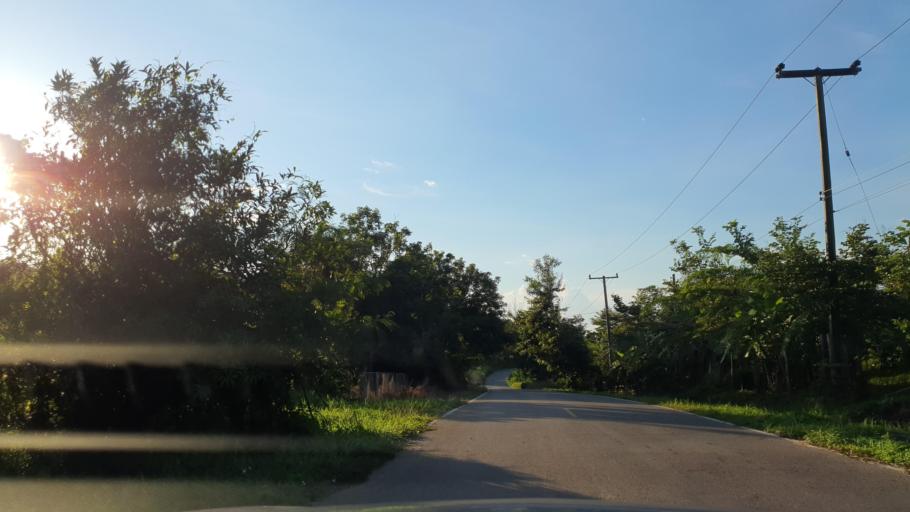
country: TH
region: Chiang Mai
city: Mae On
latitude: 18.8303
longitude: 99.2868
